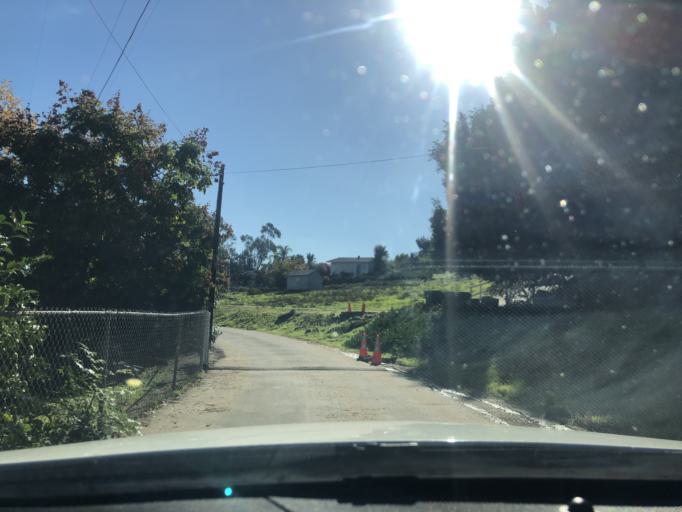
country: US
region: California
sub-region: San Diego County
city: Casa de Oro-Mount Helix
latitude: 32.7744
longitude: -116.9442
